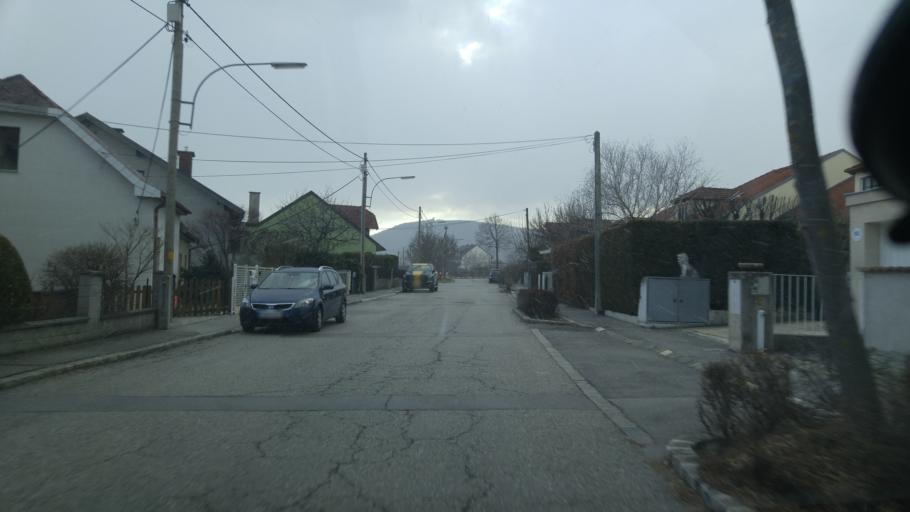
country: AT
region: Lower Austria
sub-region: Politischer Bezirk Baden
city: Baden
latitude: 47.9950
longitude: 16.2097
